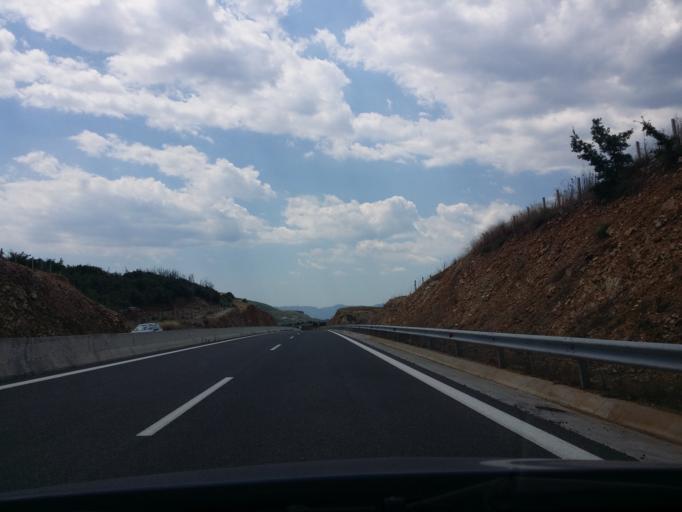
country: GR
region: Peloponnese
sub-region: Nomos Arkadias
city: Megalopoli
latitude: 37.3074
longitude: 22.1833
